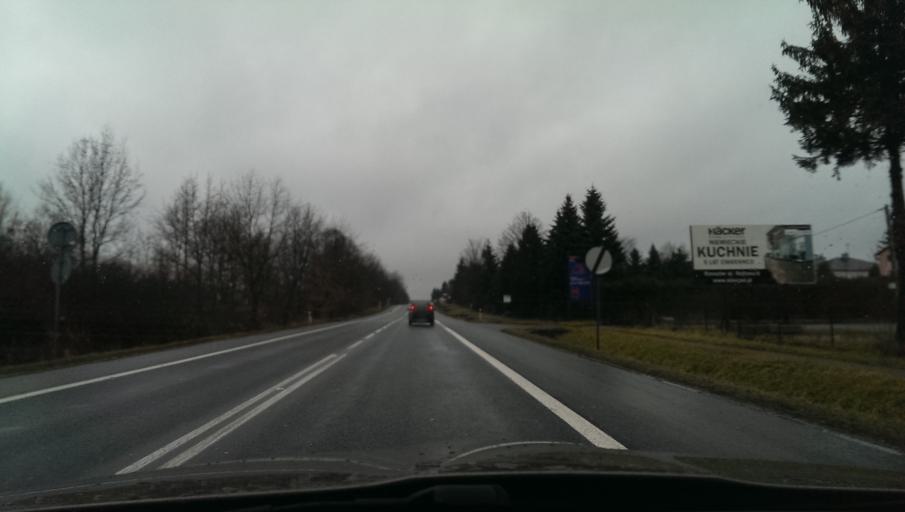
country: PL
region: Subcarpathian Voivodeship
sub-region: Powiat rzeszowski
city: Rudna Mala
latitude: 50.0998
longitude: 21.9786
